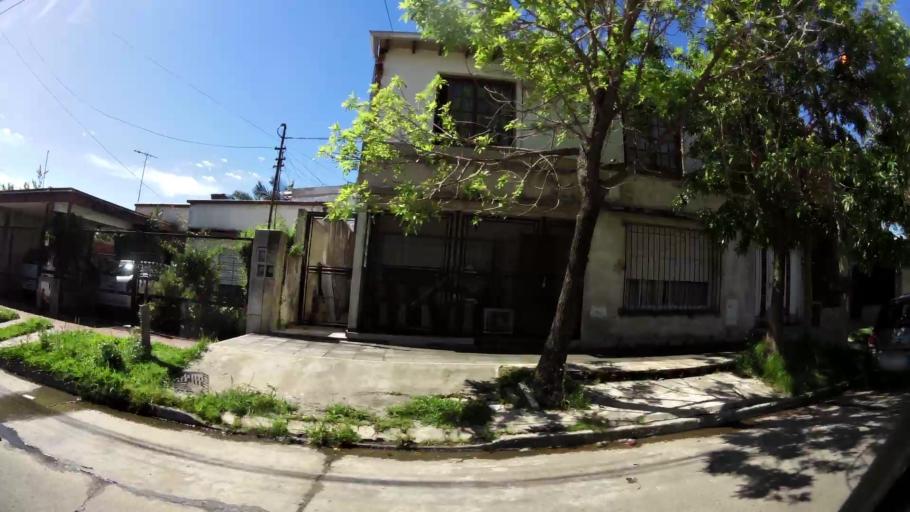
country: AR
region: Buenos Aires
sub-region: Partido de Quilmes
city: Quilmes
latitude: -34.6992
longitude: -58.2815
